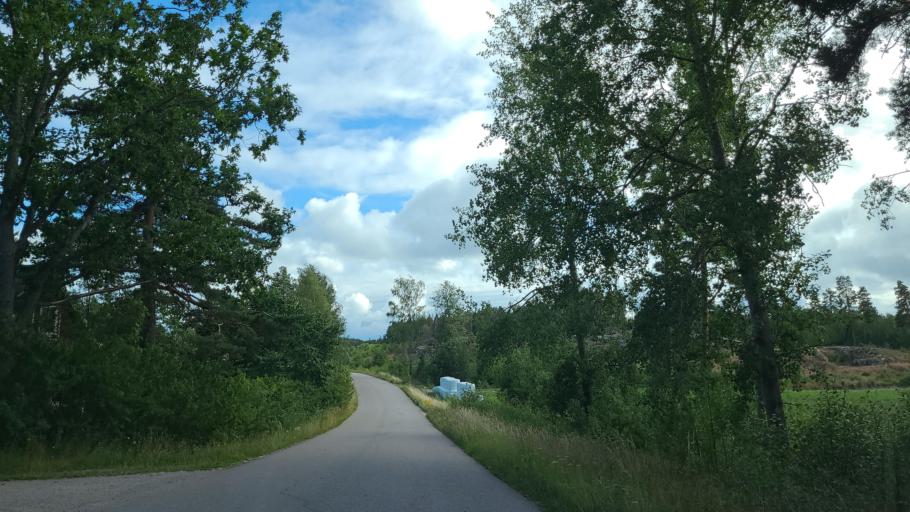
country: FI
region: Varsinais-Suomi
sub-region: Aboland-Turunmaa
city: Nagu
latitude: 60.1601
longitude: 21.7547
